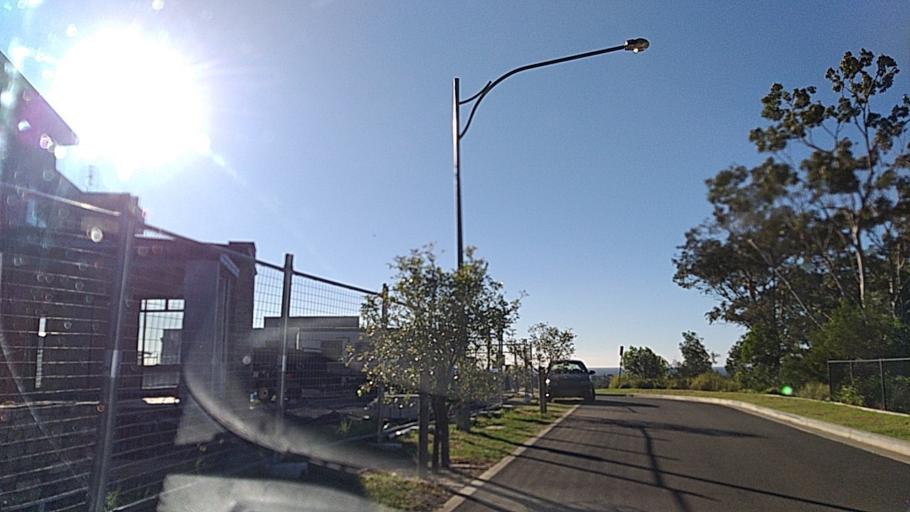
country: AU
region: New South Wales
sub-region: Wollongong
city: Bulli
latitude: -34.3332
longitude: 150.9073
